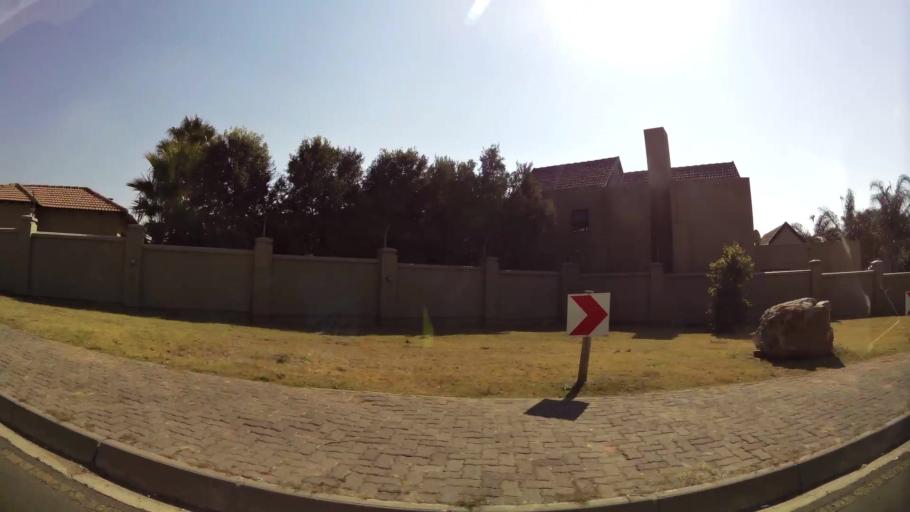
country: ZA
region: Gauteng
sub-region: City of Johannesburg Metropolitan Municipality
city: Modderfontein
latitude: -26.1140
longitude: 28.1637
